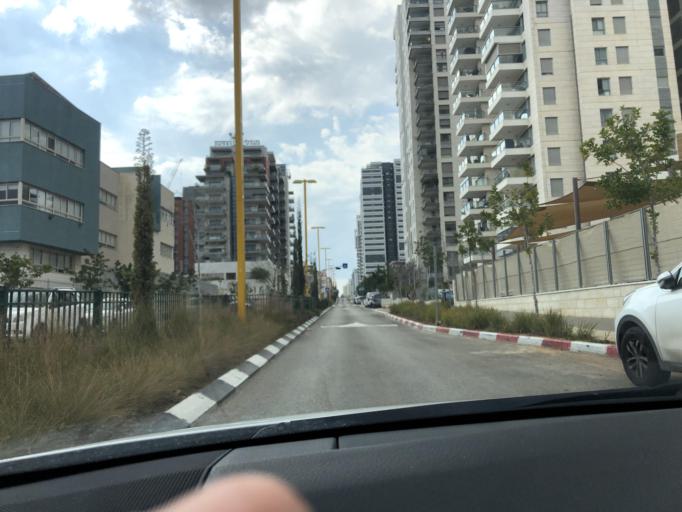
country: IL
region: Central District
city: Ganne Tiqwa
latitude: 32.0644
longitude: 34.8787
